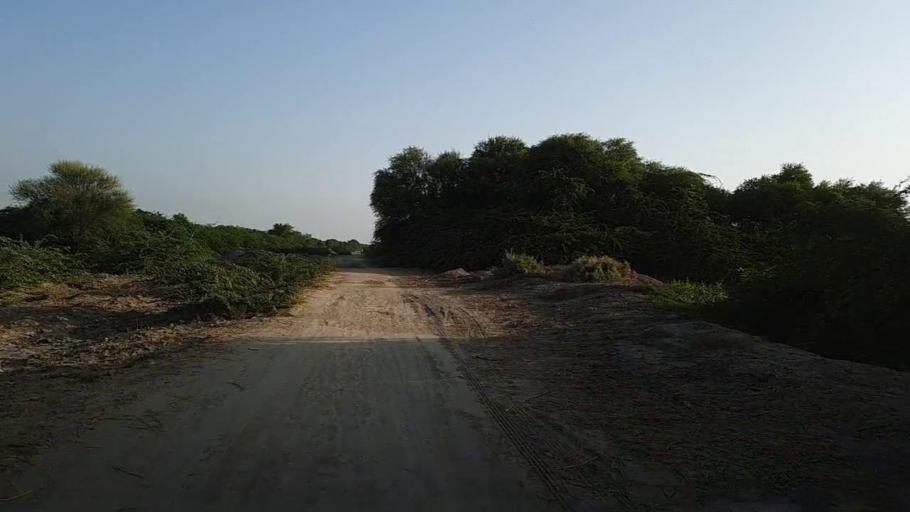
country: PK
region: Sindh
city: Kario
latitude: 24.7211
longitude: 68.6673
